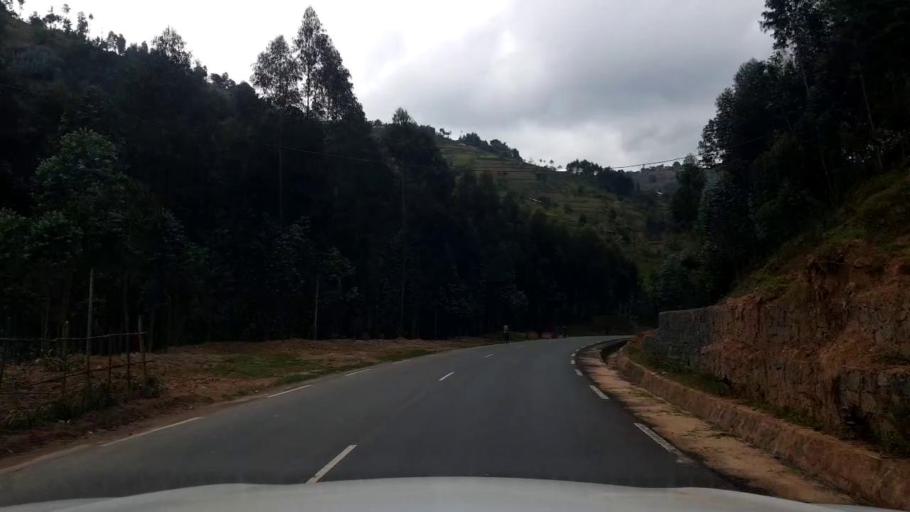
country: RW
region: Northern Province
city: Musanze
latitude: -1.6958
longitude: 29.5572
